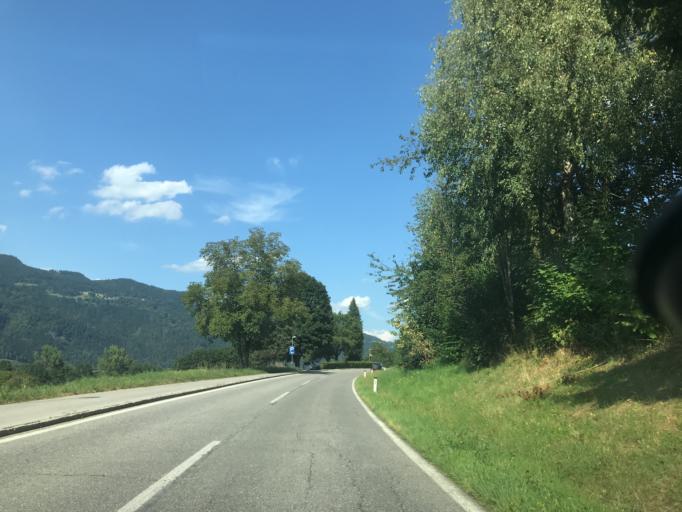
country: AT
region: Carinthia
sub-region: Politischer Bezirk Feldkirchen
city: Ossiach
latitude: 46.6784
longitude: 13.9893
